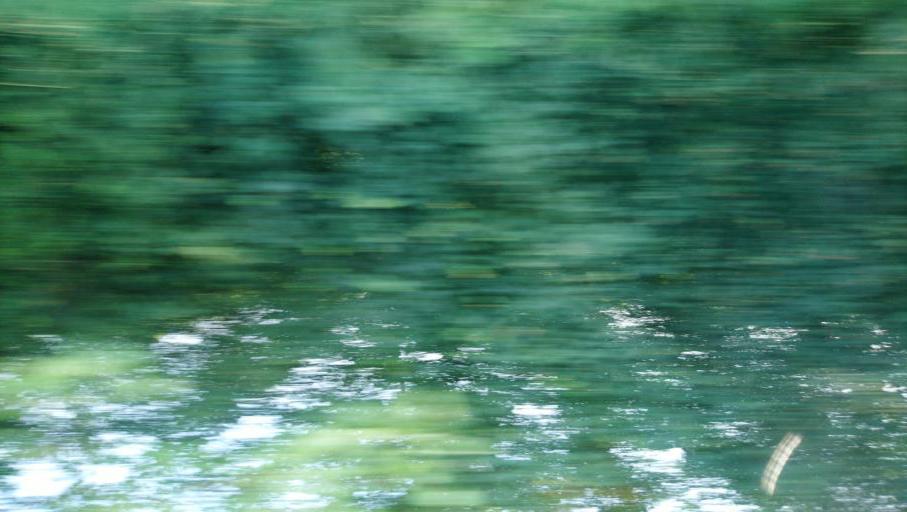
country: LU
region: Luxembourg
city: Aspelt
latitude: 49.5197
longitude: 6.2188
